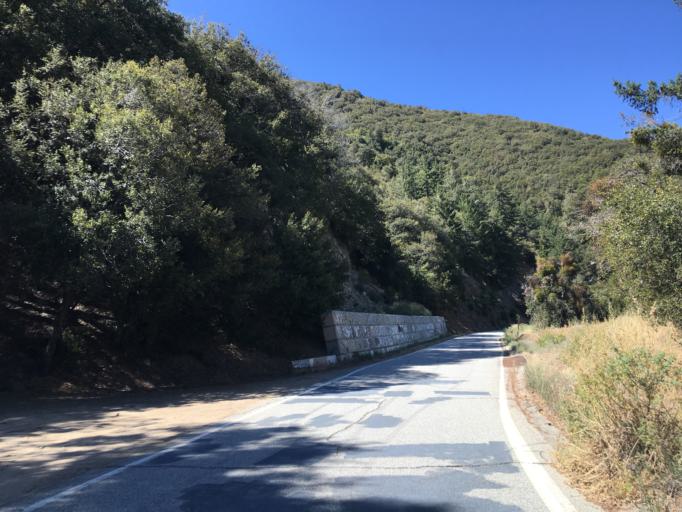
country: US
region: California
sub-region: San Bernardino County
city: San Antonio Heights
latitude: 34.2232
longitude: -117.6910
